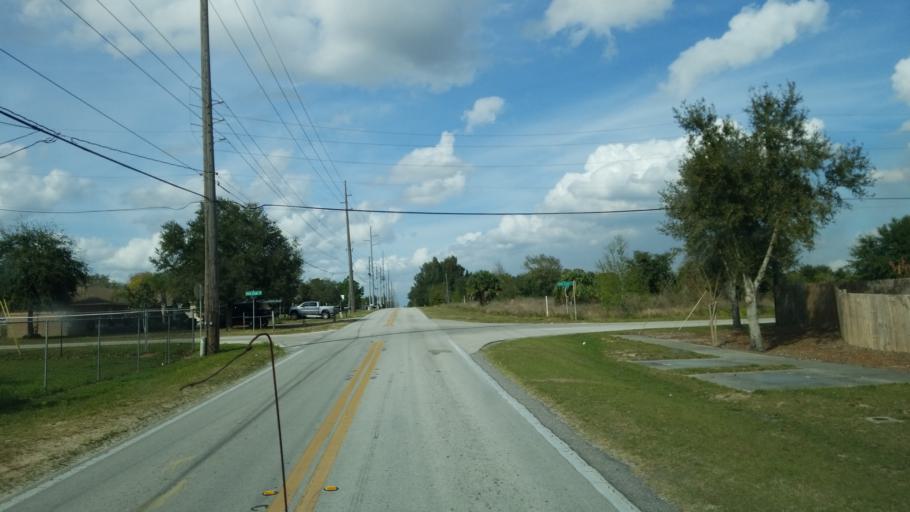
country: US
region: Florida
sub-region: Polk County
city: Davenport
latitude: 28.1425
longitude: -81.5903
